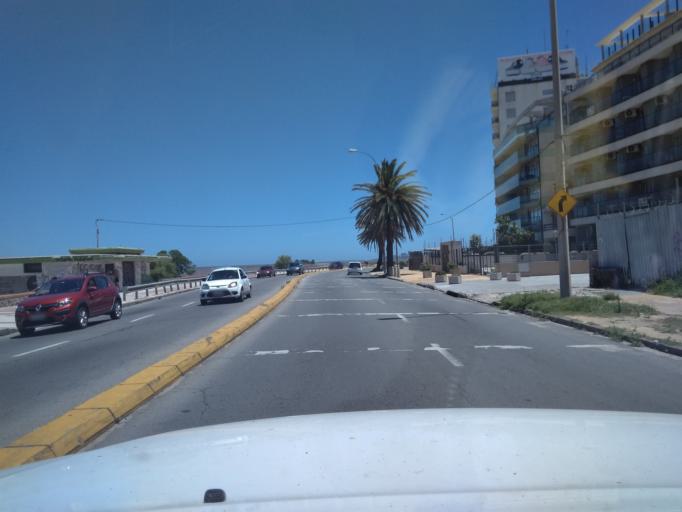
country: UY
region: Canelones
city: Paso de Carrasco
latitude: -34.8963
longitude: -56.0953
